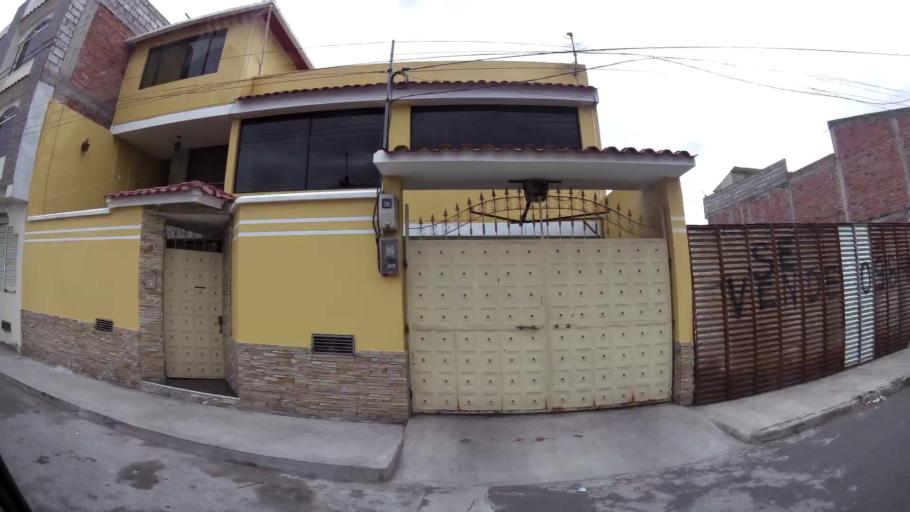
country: EC
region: Cotopaxi
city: Latacunga
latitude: -0.9376
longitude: -78.6225
